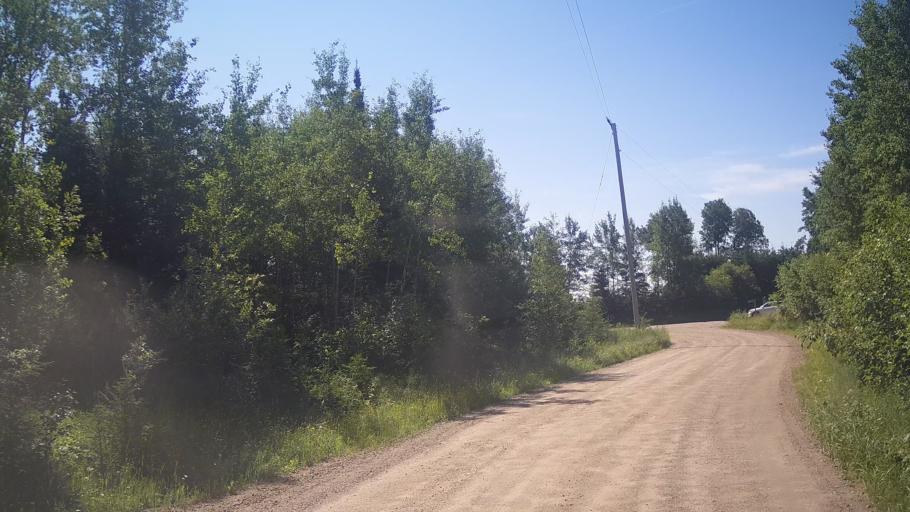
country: CA
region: Ontario
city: Dryden
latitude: 49.8159
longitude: -93.3287
